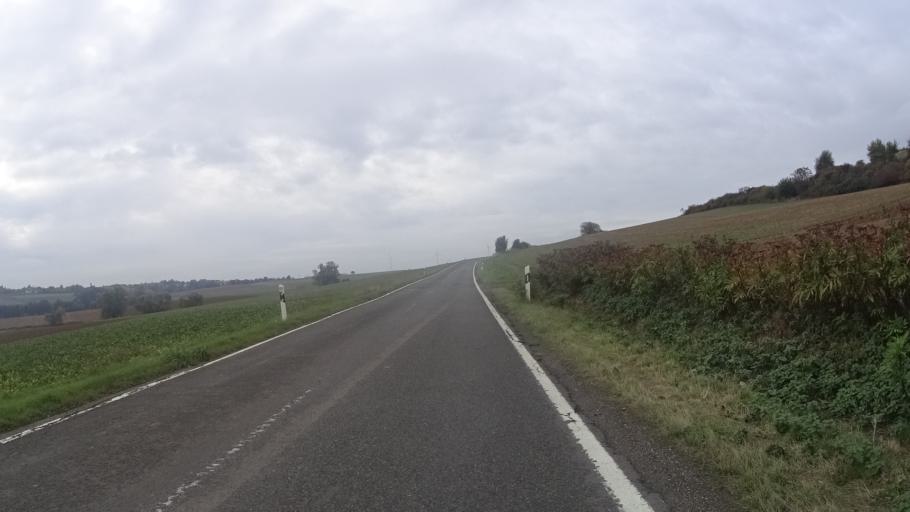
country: DE
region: Rheinland-Pfalz
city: Ottersheim
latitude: 49.6213
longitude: 8.1039
